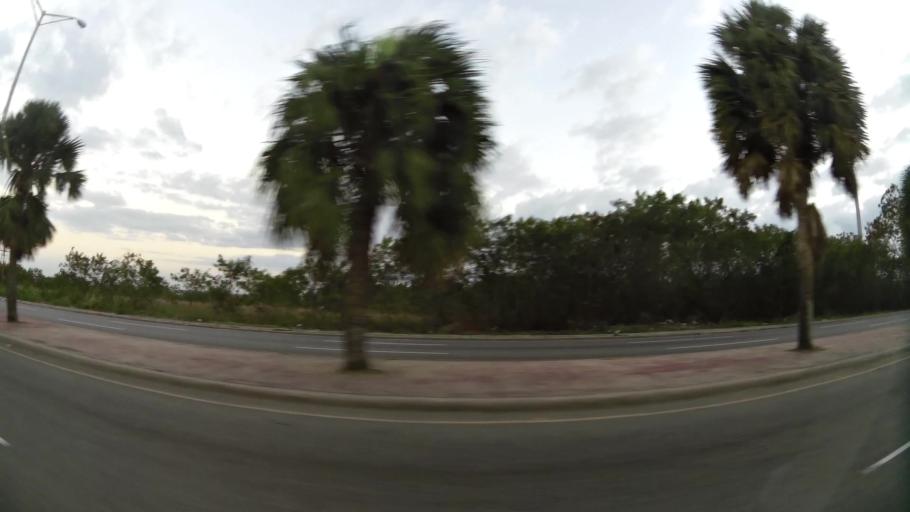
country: DO
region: Nacional
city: La Agustina
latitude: 18.5560
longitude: -69.9421
